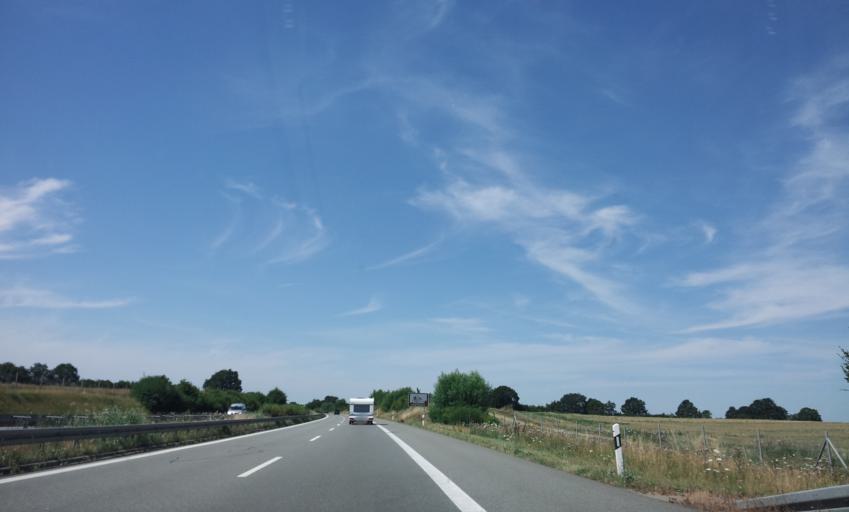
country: DE
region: Mecklenburg-Vorpommern
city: Gross Miltzow
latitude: 53.5610
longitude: 13.5100
